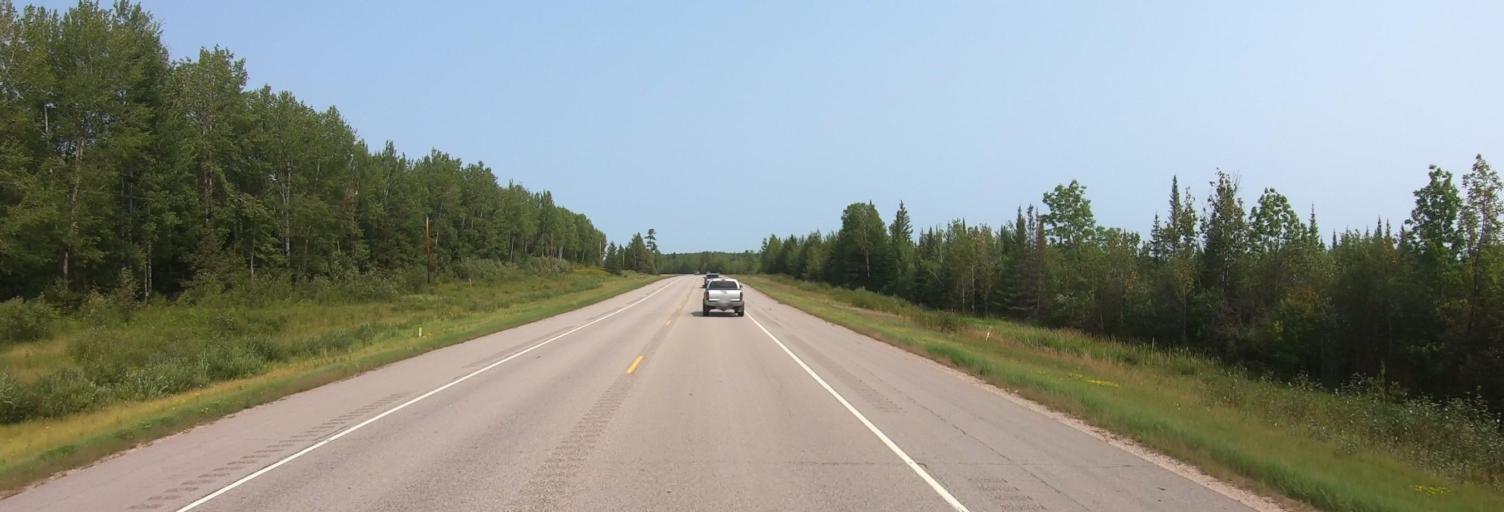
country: CA
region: Ontario
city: Fort Frances
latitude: 48.3220
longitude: -92.9617
